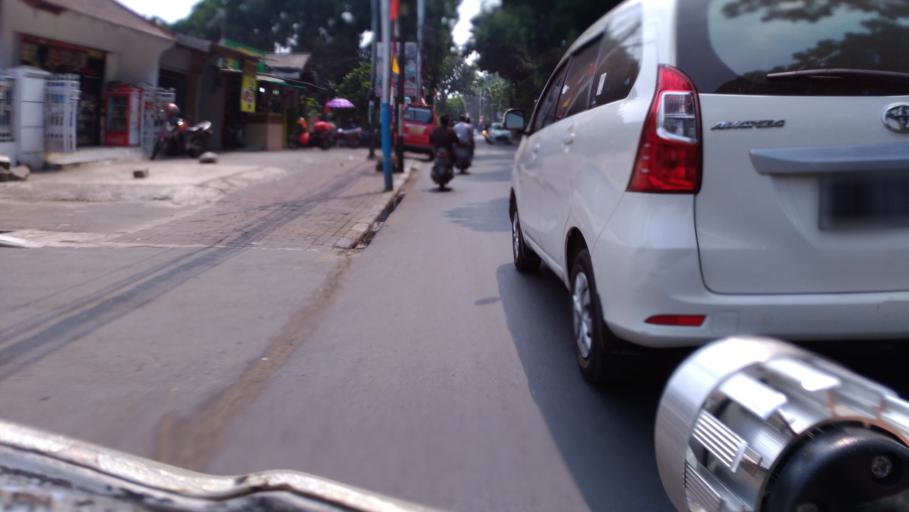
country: ID
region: West Java
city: Cileungsir
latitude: -6.3195
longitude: 106.8901
